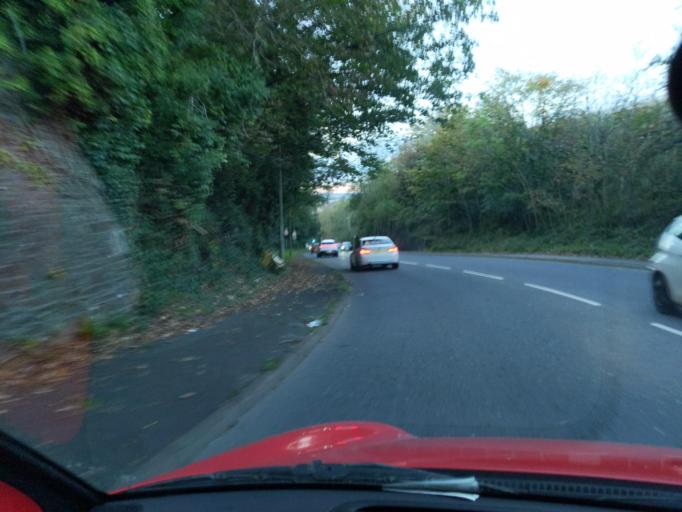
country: GB
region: England
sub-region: Plymouth
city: Plymouth
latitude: 50.4165
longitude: -4.1360
